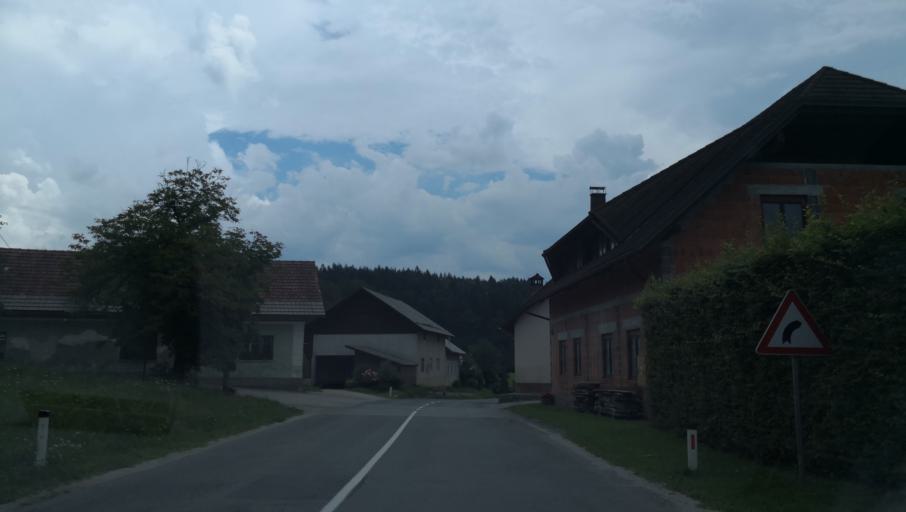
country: SI
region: Ivancna Gorica
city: Ivancna Gorica
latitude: 45.8812
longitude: 14.7965
